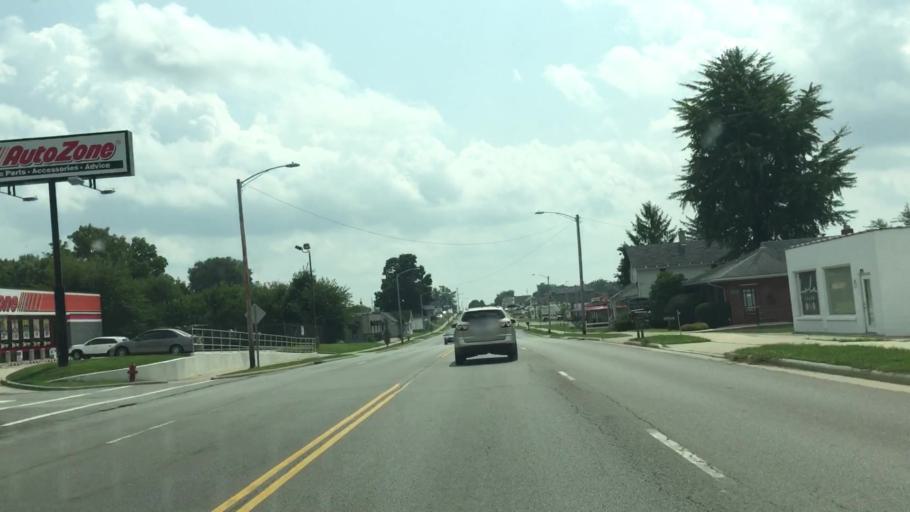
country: US
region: Ohio
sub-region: Logan County
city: Bellefontaine
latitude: 40.3443
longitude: -83.7615
